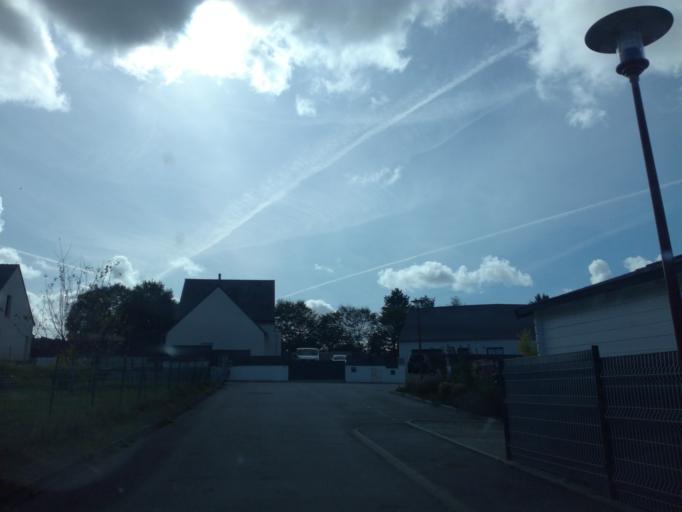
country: FR
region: Brittany
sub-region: Departement du Morbihan
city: Le Sourn
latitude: 48.0438
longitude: -2.9832
